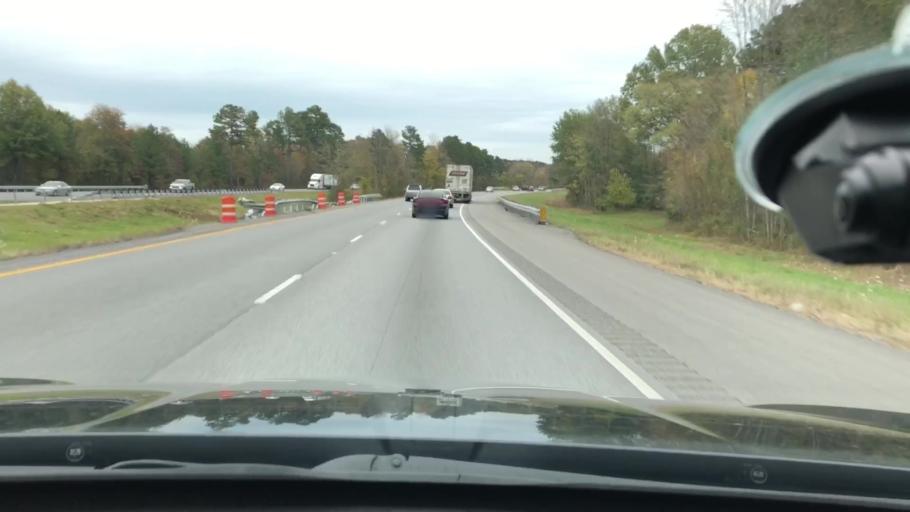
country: US
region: Arkansas
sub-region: Hempstead County
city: Hope
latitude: 33.6200
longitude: -93.7878
